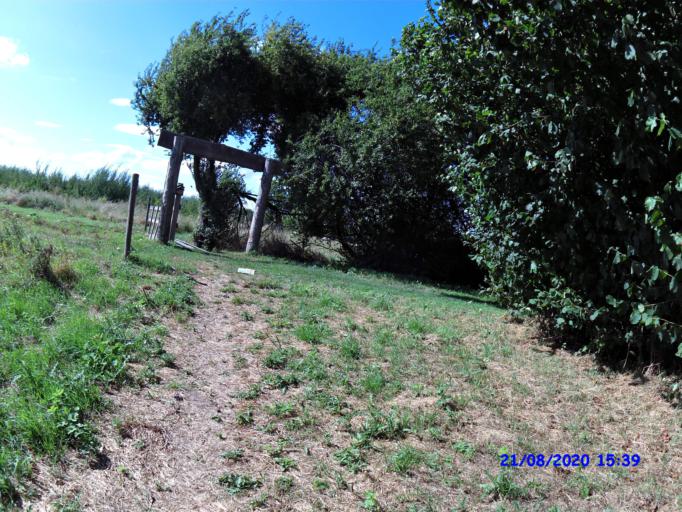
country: BE
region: Flanders
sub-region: Provincie Limburg
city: Sint-Truiden
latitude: 50.8167
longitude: 5.1639
